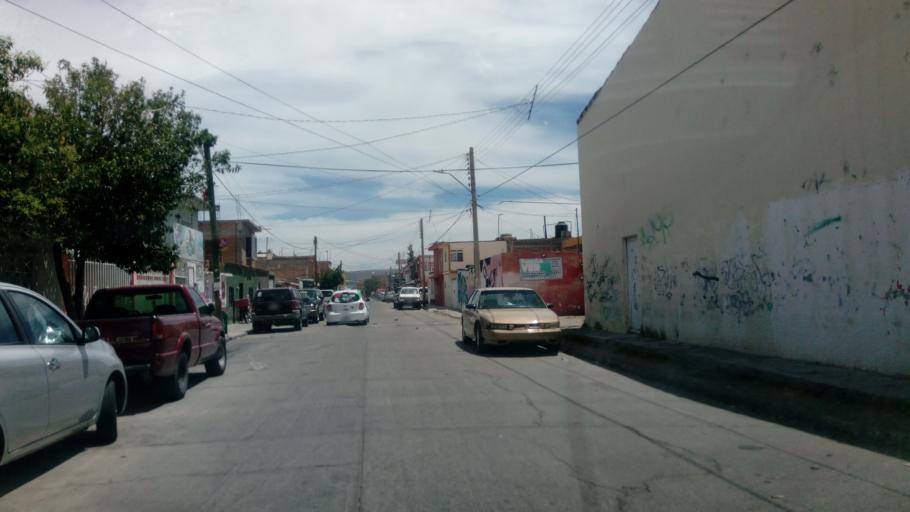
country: MX
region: Durango
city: Victoria de Durango
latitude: 24.0024
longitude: -104.6774
